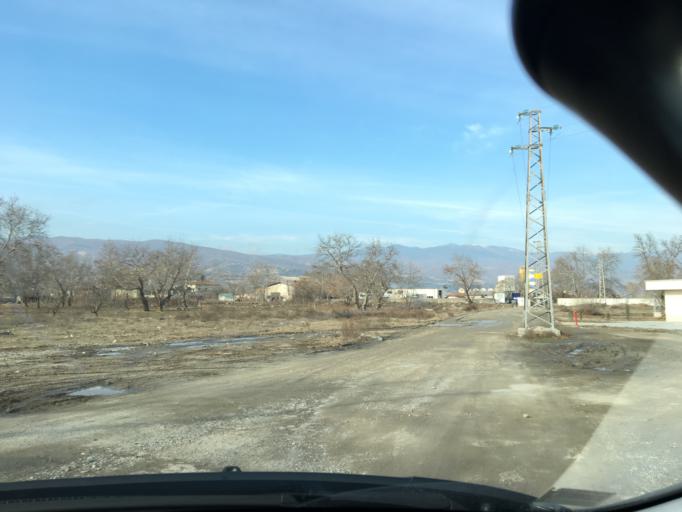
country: BG
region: Blagoevgrad
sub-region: Obshtina Strumyani
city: Strumyani
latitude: 41.6273
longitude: 23.2016
